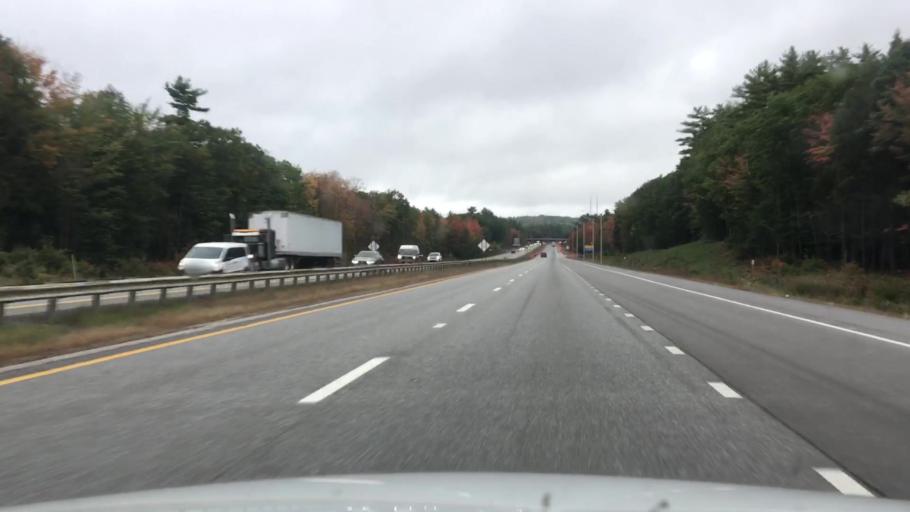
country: US
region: Maine
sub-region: Cumberland County
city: Cumberland Center
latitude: 43.8279
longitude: -70.3218
